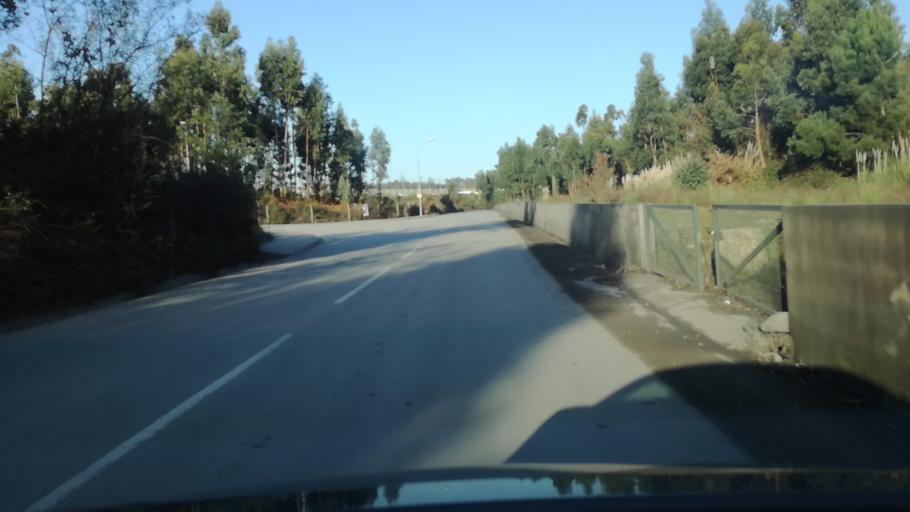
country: PT
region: Braga
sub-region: Vila Nova de Famalicao
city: Ferreiros
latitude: 41.3632
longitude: -8.5361
